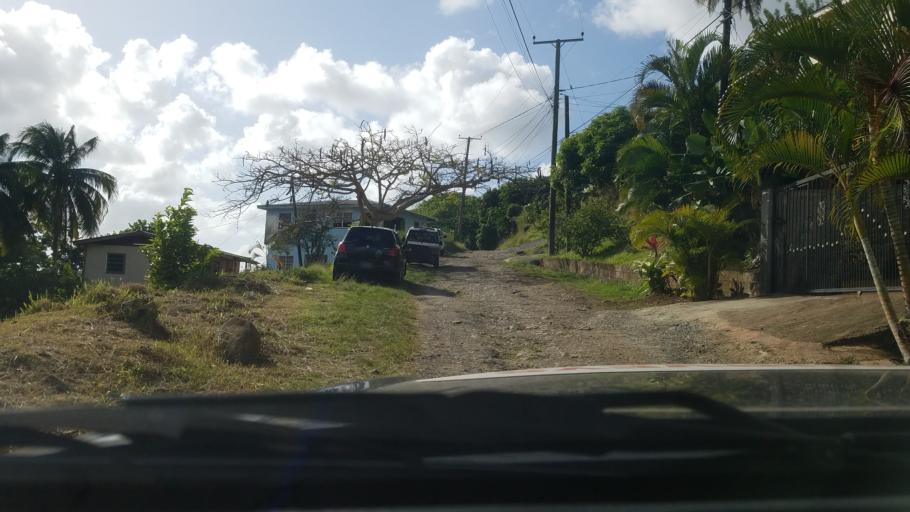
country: LC
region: Castries Quarter
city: Bisee
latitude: 14.0374
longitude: -60.9492
